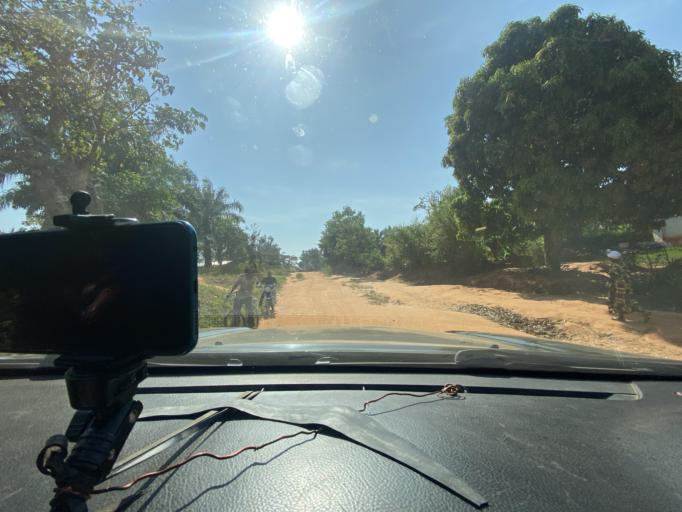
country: CD
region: Kasai-Oriental
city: Kabinda
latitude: -6.1309
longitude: 24.5146
